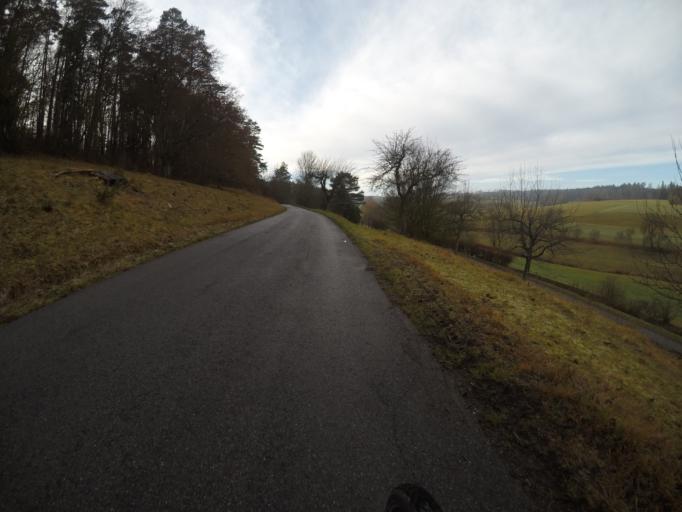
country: DE
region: Baden-Wuerttemberg
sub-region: Karlsruhe Region
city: Gechingen
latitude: 48.6774
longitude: 8.8437
